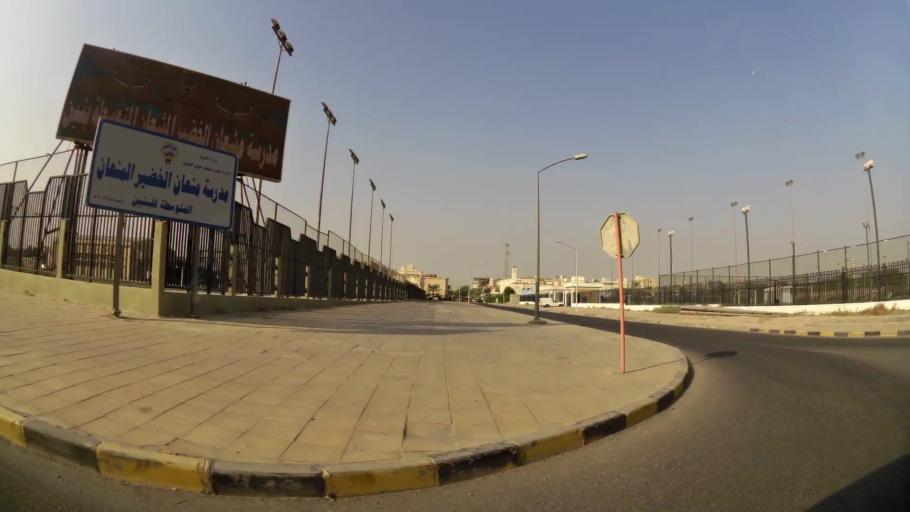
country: KW
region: Muhafazat Hawalli
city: Salwa
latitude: 29.2877
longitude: 48.0667
